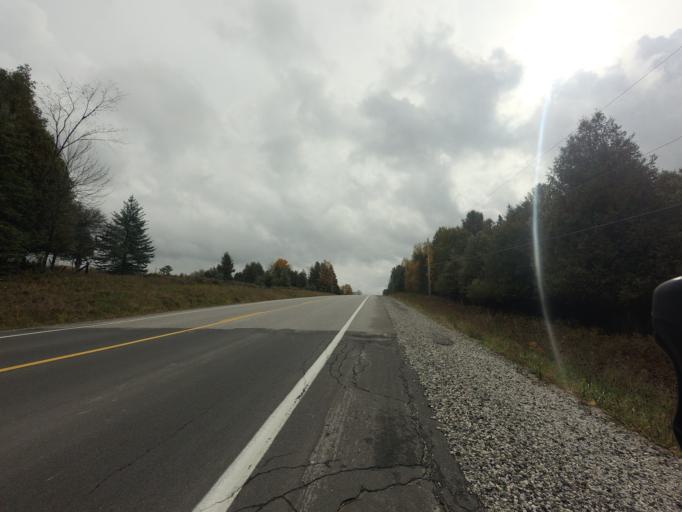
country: CA
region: Ontario
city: Perth
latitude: 45.1014
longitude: -76.4703
